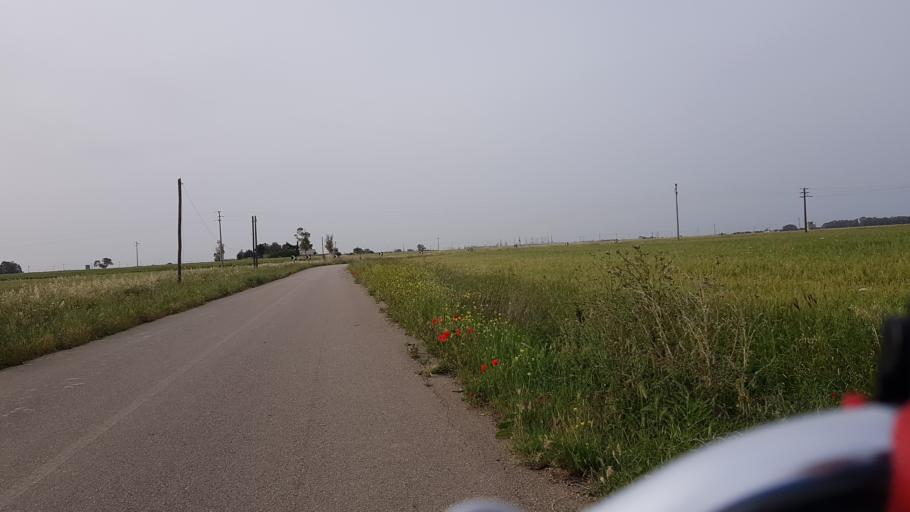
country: IT
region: Apulia
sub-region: Provincia di Brindisi
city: La Rosa
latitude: 40.5732
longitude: 18.0141
